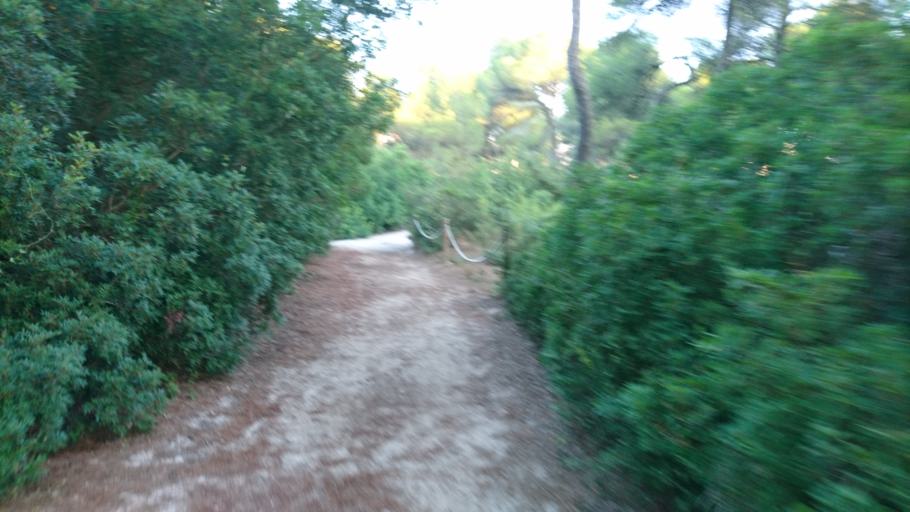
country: ES
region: Balearic Islands
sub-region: Illes Balears
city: Port d'Alcudia
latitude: 39.7855
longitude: 3.1291
